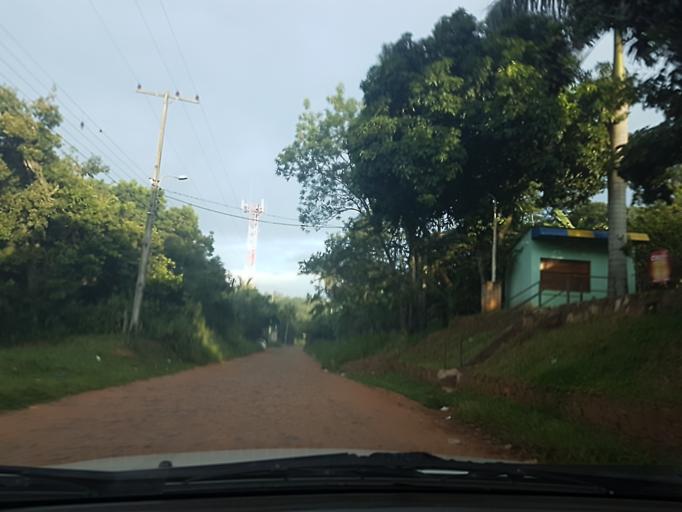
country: PY
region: Central
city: Limpio
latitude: -25.2407
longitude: -57.4594
